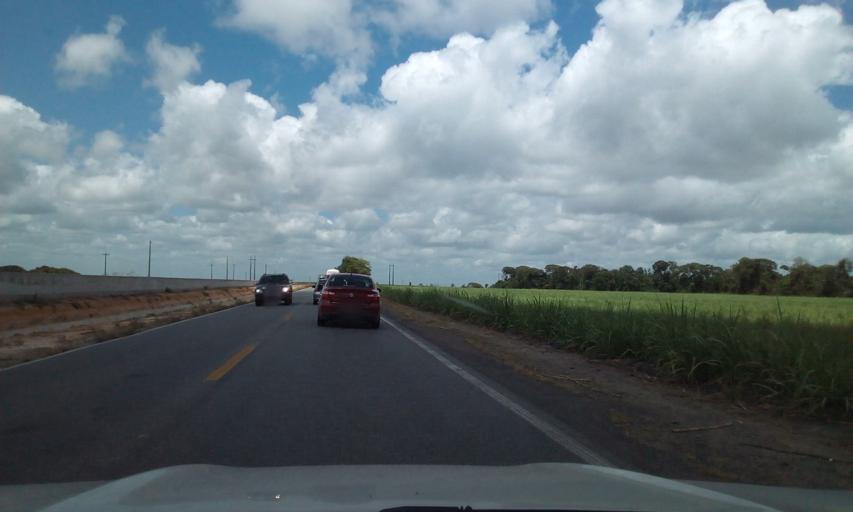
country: BR
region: Alagoas
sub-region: Pilar
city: Pilar
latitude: -9.6123
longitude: -36.0278
